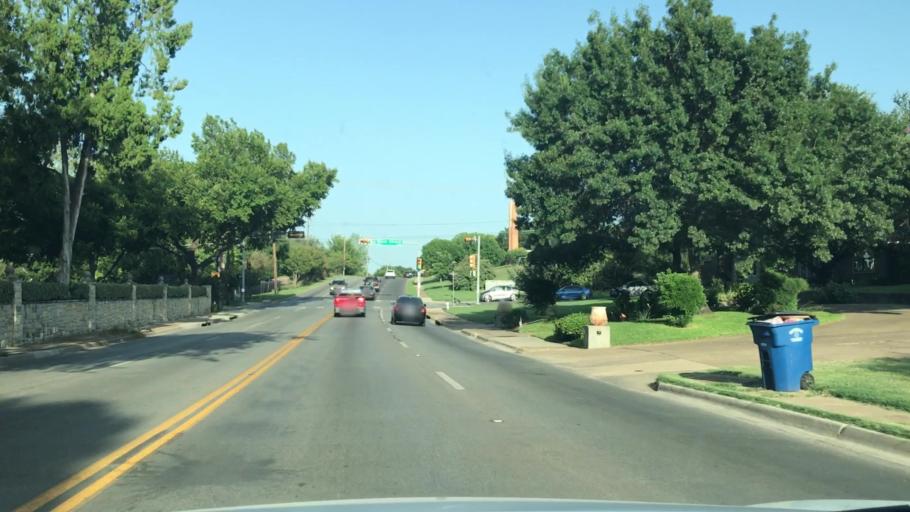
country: US
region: Texas
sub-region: Dallas County
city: Highland Park
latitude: 32.8153
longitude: -96.7383
